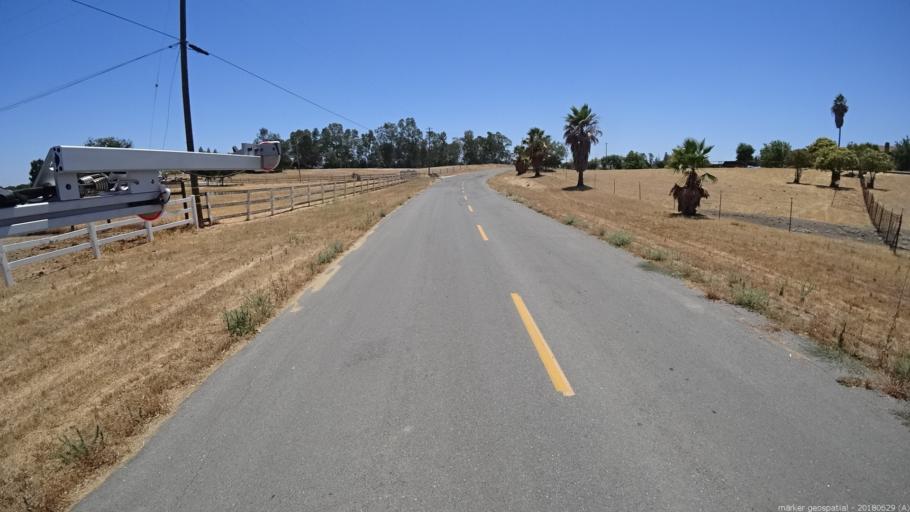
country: US
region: California
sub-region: Madera County
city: Parksdale
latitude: 37.0036
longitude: -119.9764
